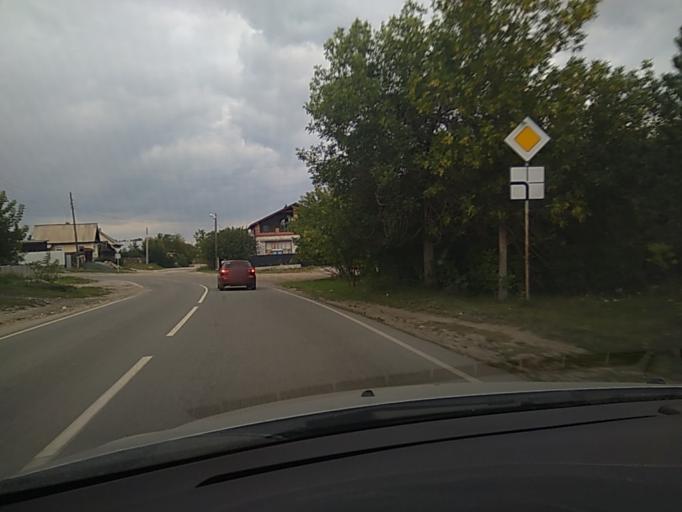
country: RU
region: Chelyabinsk
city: Kyshtym
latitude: 55.7124
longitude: 60.5135
